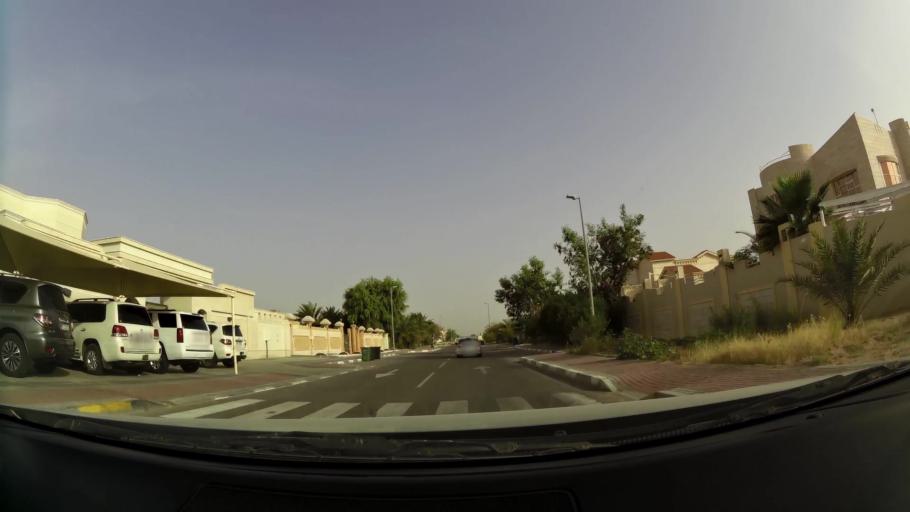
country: AE
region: Abu Dhabi
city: Al Ain
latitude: 24.1249
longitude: 55.6949
